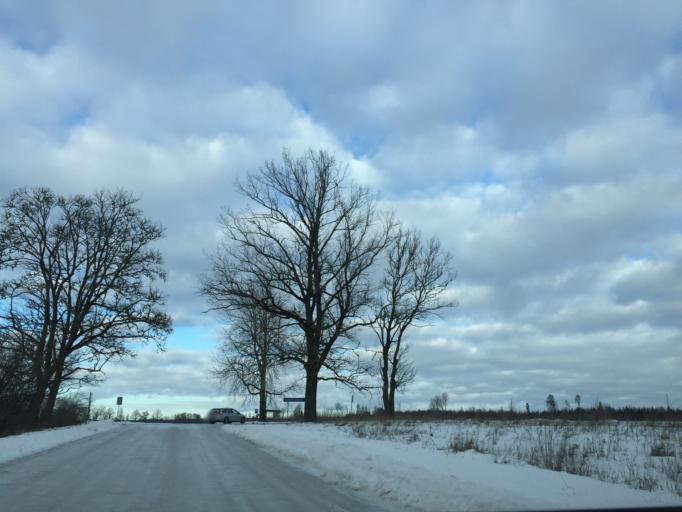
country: LV
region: Lielvarde
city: Lielvarde
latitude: 56.5827
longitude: 24.7347
